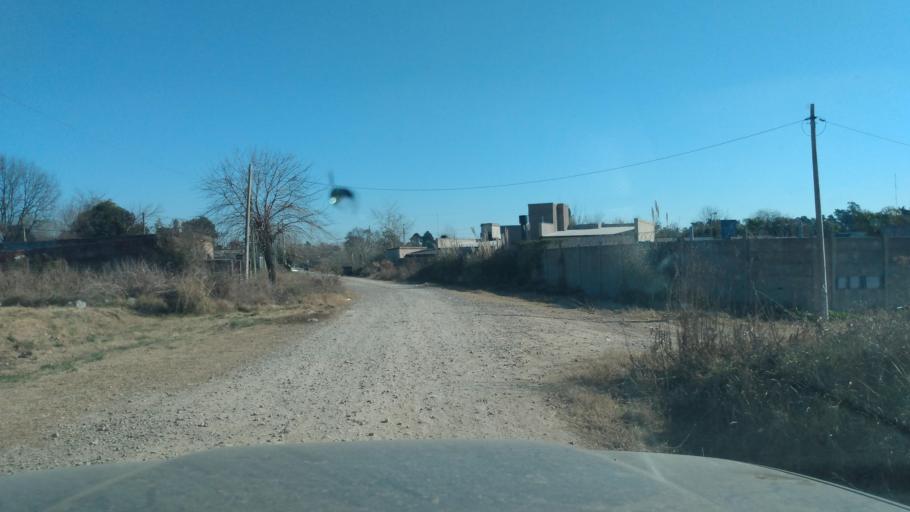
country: AR
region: Buenos Aires
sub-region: Partido de Lujan
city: Lujan
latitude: -34.5664
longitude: -59.0865
